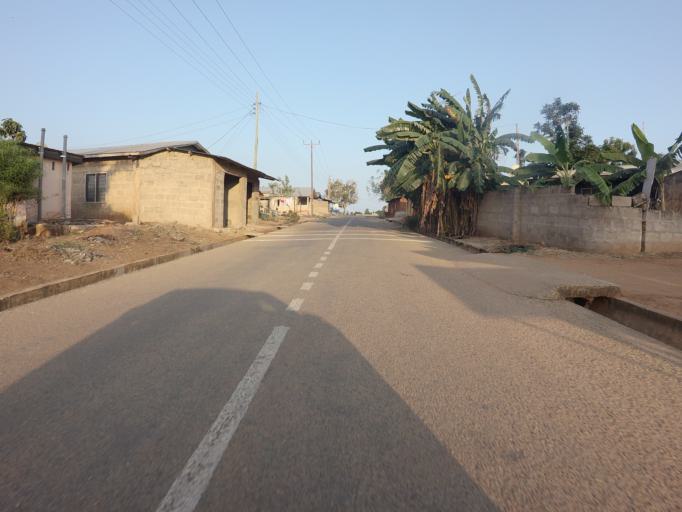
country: GH
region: Volta
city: Anloga
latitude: 6.0050
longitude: 0.5964
